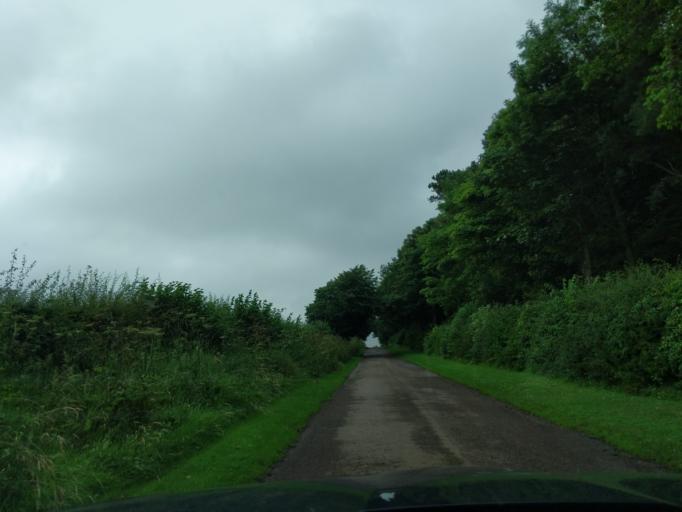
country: GB
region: England
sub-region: Northumberland
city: Ford
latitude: 55.6805
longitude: -2.1210
